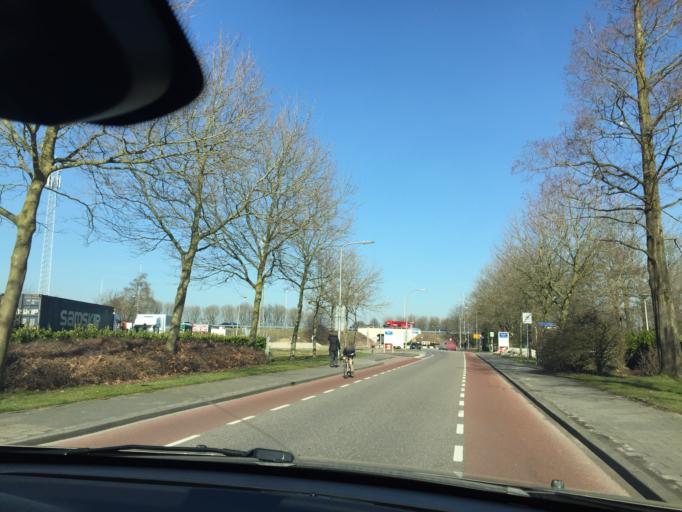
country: NL
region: Utrecht
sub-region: Gemeente Oudewater
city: Oudewater
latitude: 52.0637
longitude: 4.8215
